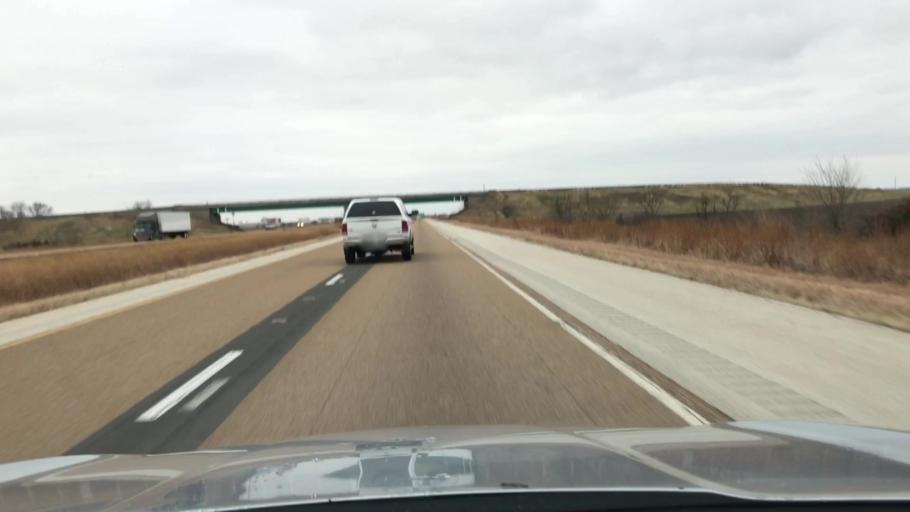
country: US
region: Illinois
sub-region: Montgomery County
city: Litchfield
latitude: 39.1920
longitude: -89.6697
